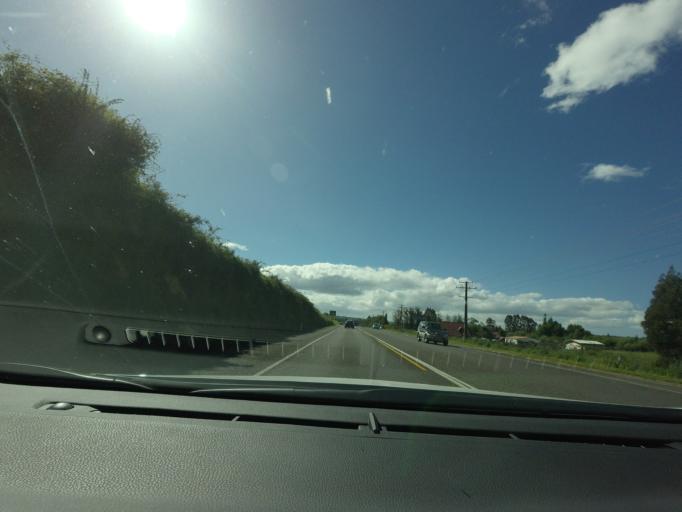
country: NZ
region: Bay of Plenty
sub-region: Rotorua District
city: Rotorua
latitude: -38.0934
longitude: 176.2167
